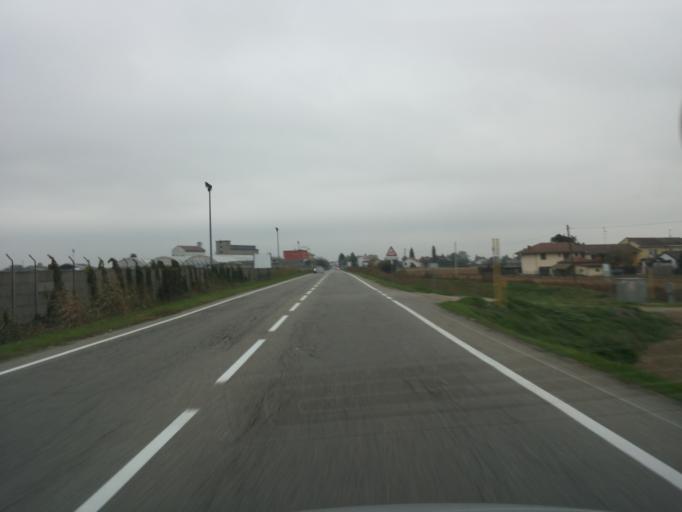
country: IT
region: Piedmont
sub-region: Provincia di Vercelli
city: Borgo Vercelli
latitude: 45.3318
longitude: 8.4488
